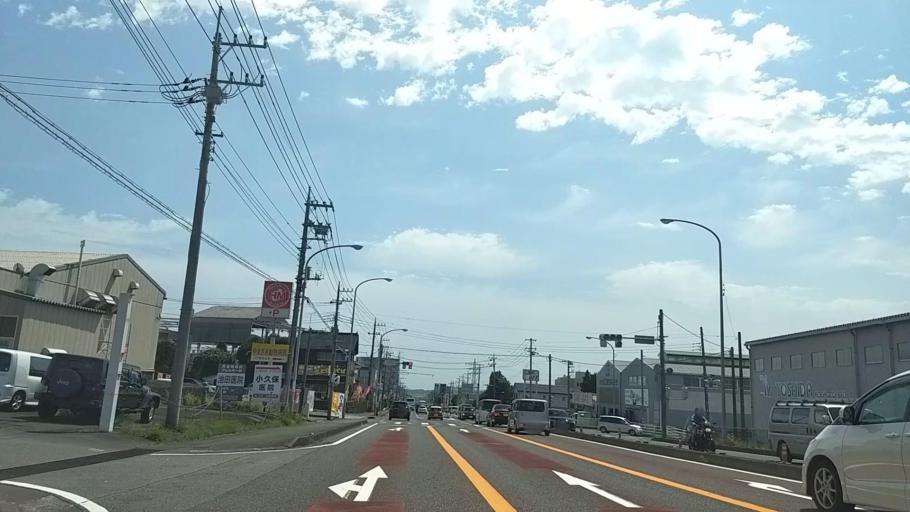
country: JP
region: Shizuoka
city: Fujinomiya
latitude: 35.2461
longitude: 138.6179
